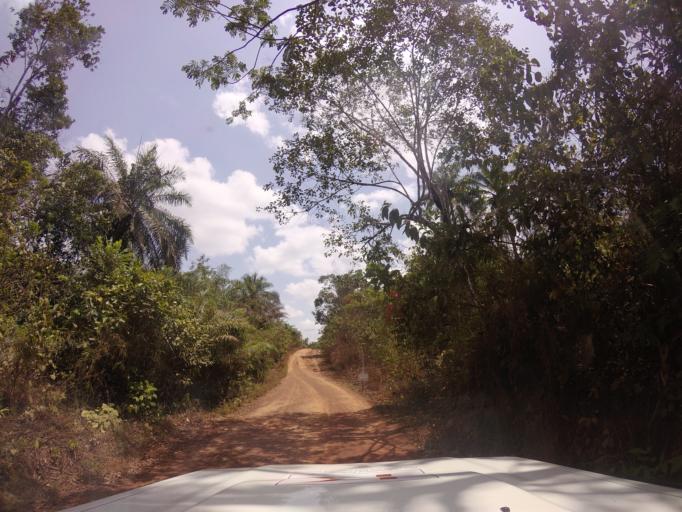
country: SL
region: Southern Province
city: Zimmi
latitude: 7.1900
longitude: -11.2242
